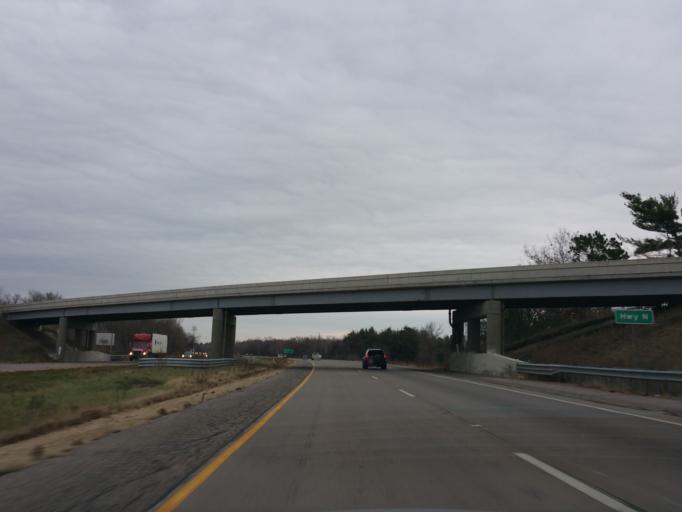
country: US
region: Wisconsin
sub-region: Juneau County
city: Mauston
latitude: 43.7849
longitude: -90.0442
